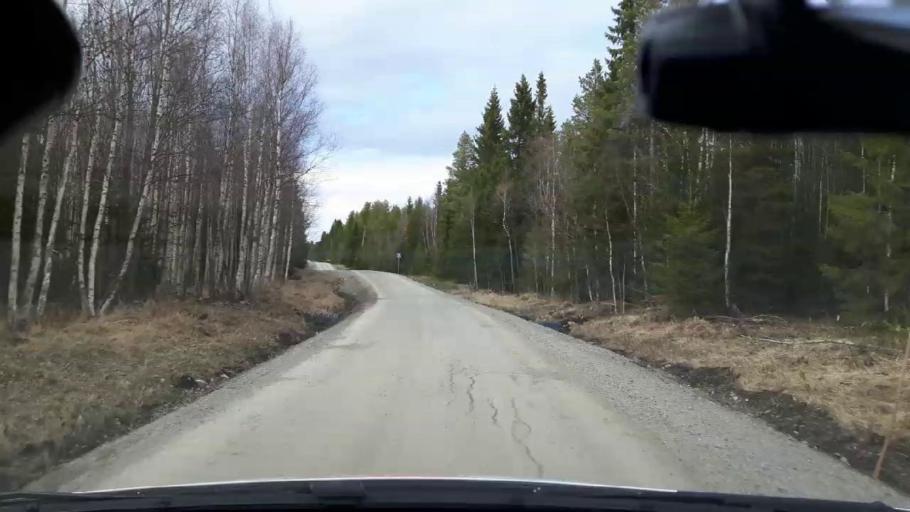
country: SE
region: Jaemtland
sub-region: OEstersunds Kommun
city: Brunflo
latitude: 62.9363
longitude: 14.6640
